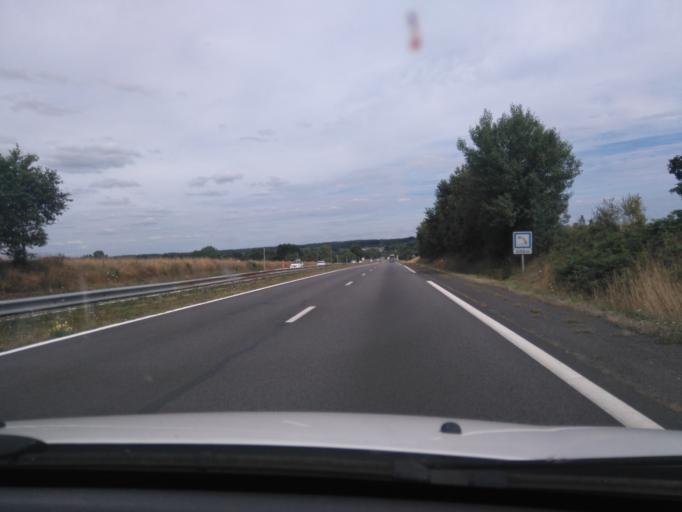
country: FR
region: Brittany
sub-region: Departement d'Ille-et-Vilaine
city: Montauban-de-Bretagne
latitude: 48.2079
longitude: -2.0625
